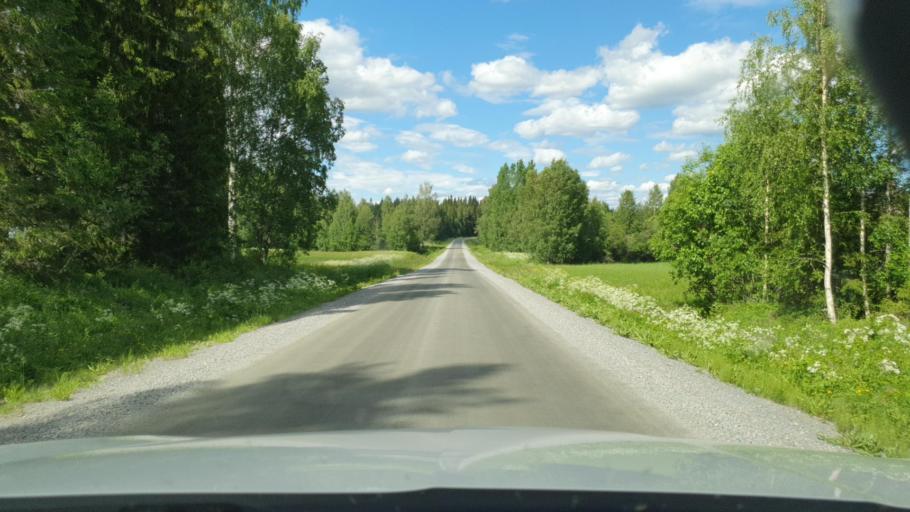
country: SE
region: Vaesterbotten
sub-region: Skelleftea Kommun
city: Forsbacka
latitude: 64.8111
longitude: 20.4957
